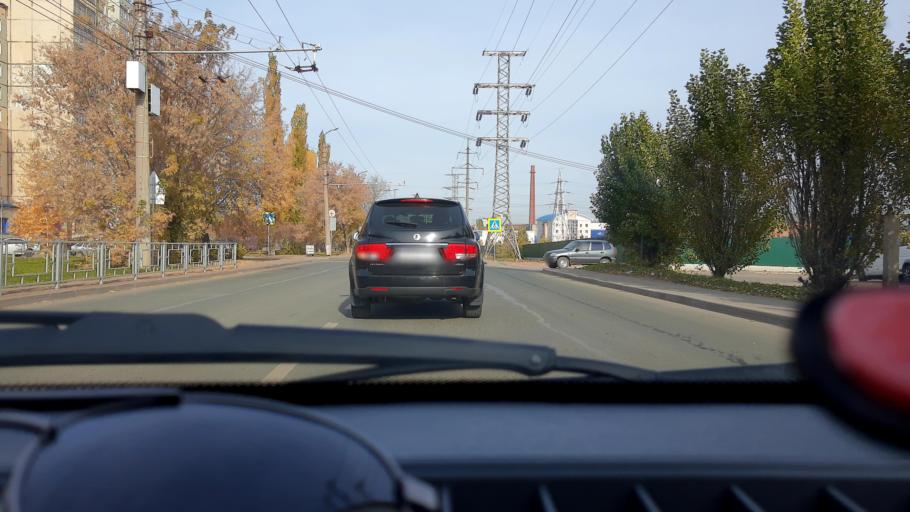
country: RU
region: Bashkortostan
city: Ufa
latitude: 54.7948
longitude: 56.0561
